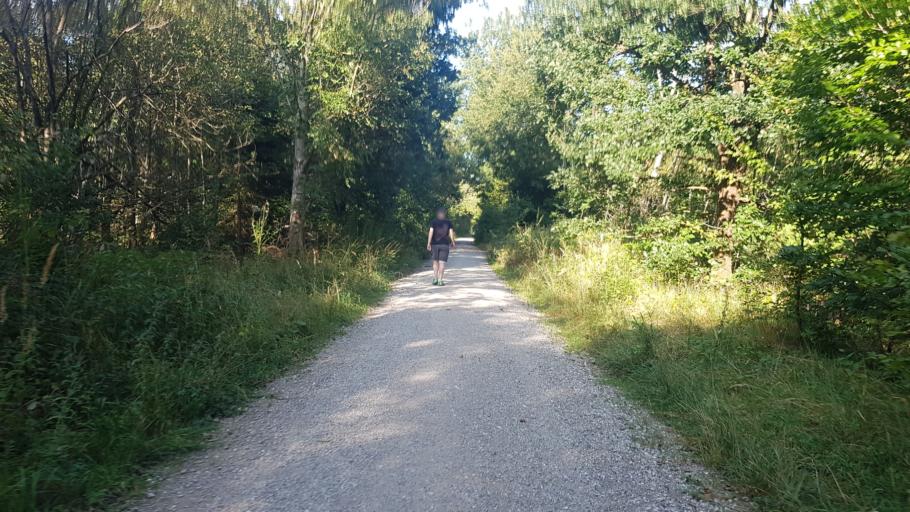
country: DE
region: Bavaria
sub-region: Upper Bavaria
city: Krailling
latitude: 48.0976
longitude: 11.3927
